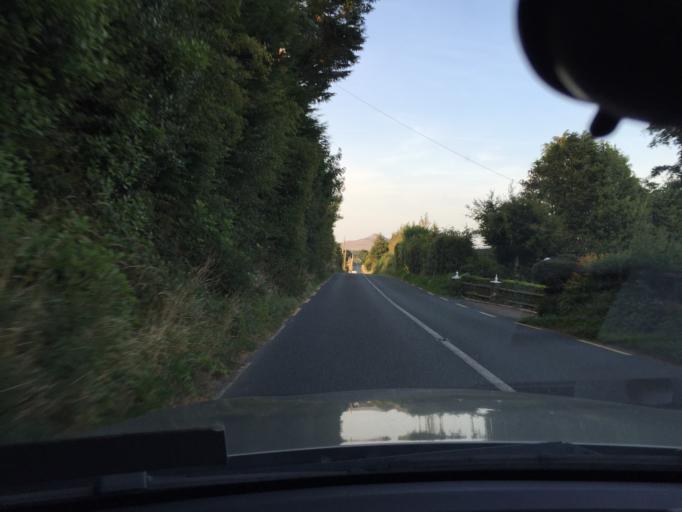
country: IE
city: Newtownmountkennedy
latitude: 53.1058
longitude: -6.1941
